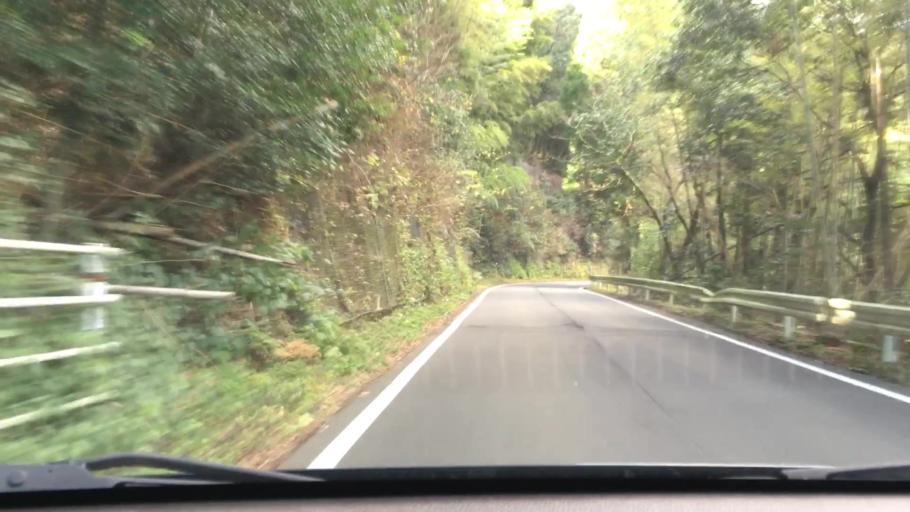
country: JP
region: Kagoshima
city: Ijuin
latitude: 31.7171
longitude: 130.4315
